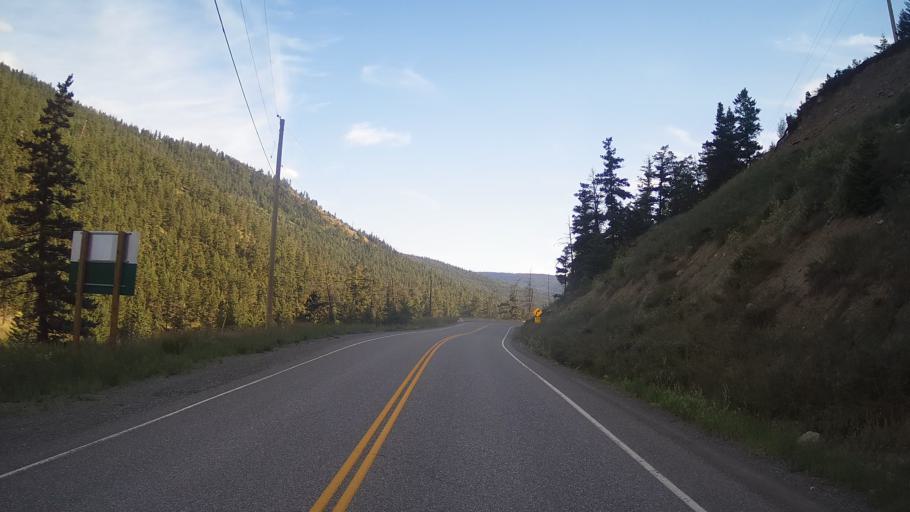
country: CA
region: British Columbia
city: Cache Creek
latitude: 50.8650
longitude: -121.5266
